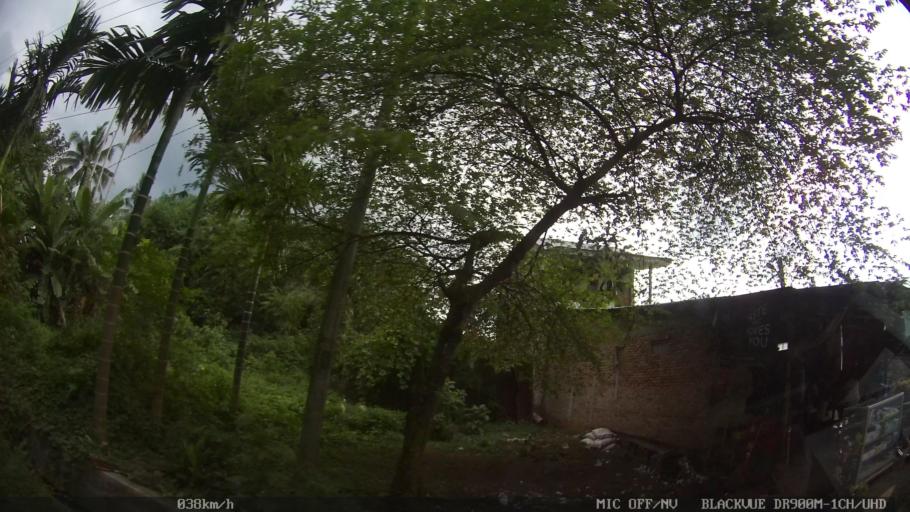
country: ID
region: North Sumatra
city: Sunggal
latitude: 3.5296
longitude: 98.6076
